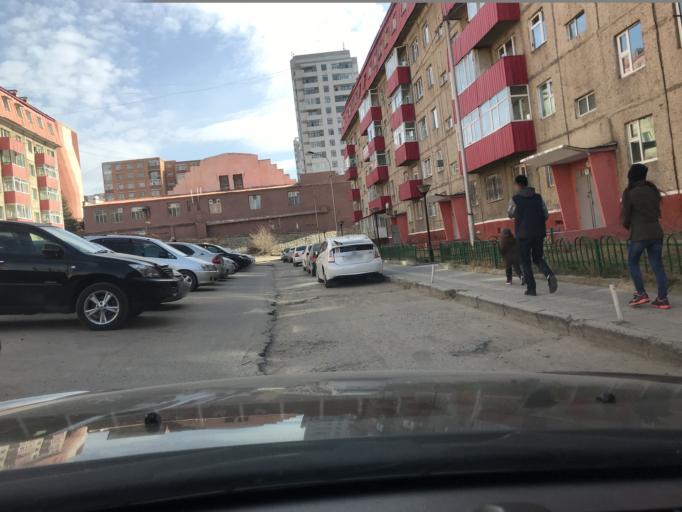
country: MN
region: Ulaanbaatar
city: Ulaanbaatar
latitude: 47.9209
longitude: 106.9440
